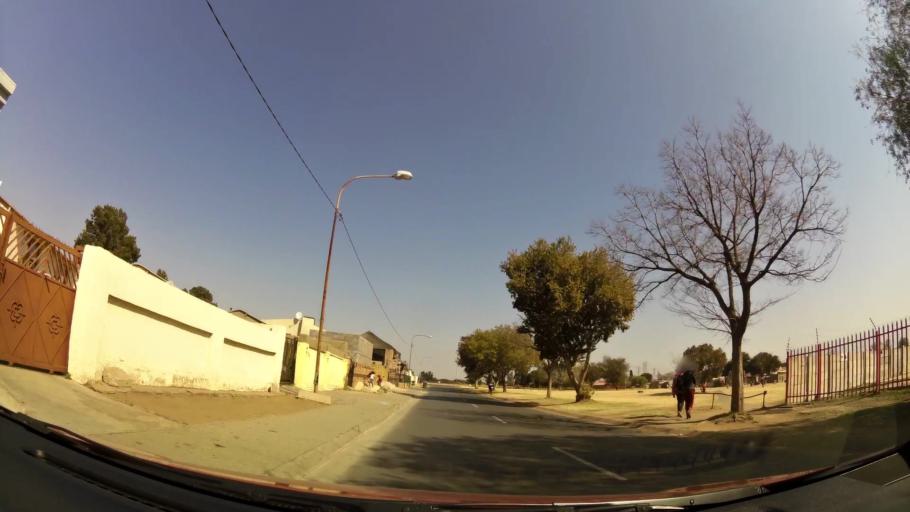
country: ZA
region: Gauteng
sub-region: City of Johannesburg Metropolitan Municipality
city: Soweto
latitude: -26.2399
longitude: 27.9417
